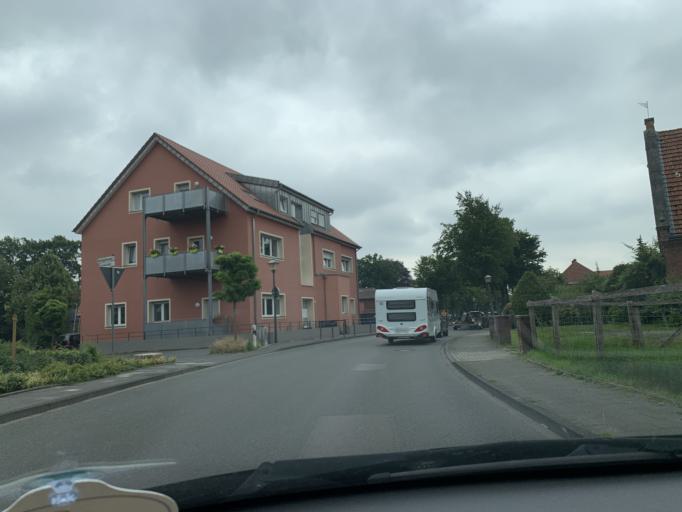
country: DE
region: North Rhine-Westphalia
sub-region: Regierungsbezirk Munster
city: Ostbevern
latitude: 52.0412
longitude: 7.8407
